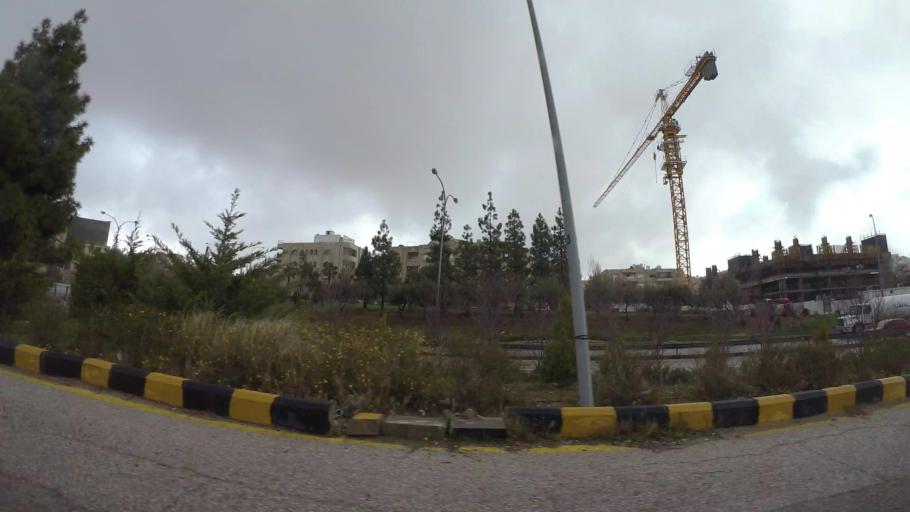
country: JO
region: Amman
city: Wadi as Sir
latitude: 31.9446
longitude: 35.8587
